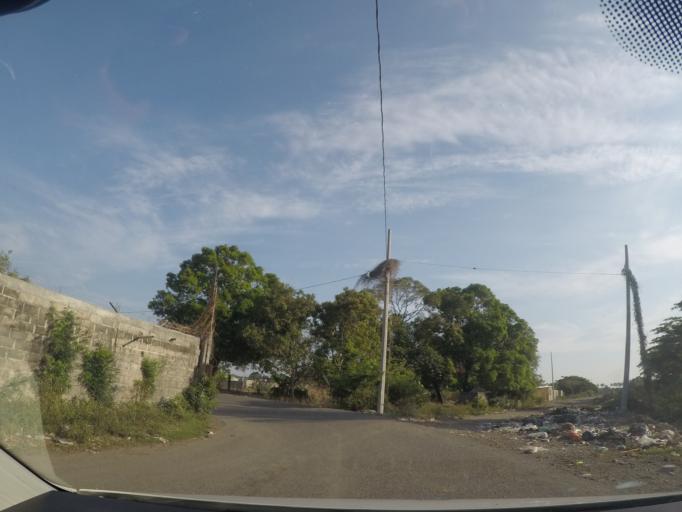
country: MX
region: Oaxaca
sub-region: Santo Domingo Tehuantepec
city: La Noria
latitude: 16.2485
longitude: -95.1491
